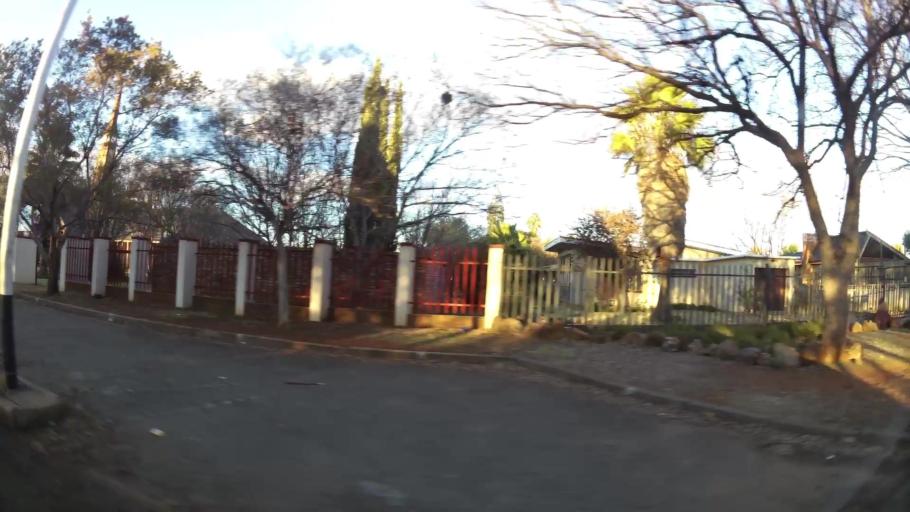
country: ZA
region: North-West
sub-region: Dr Kenneth Kaunda District Municipality
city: Potchefstroom
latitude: -26.7309
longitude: 27.0859
